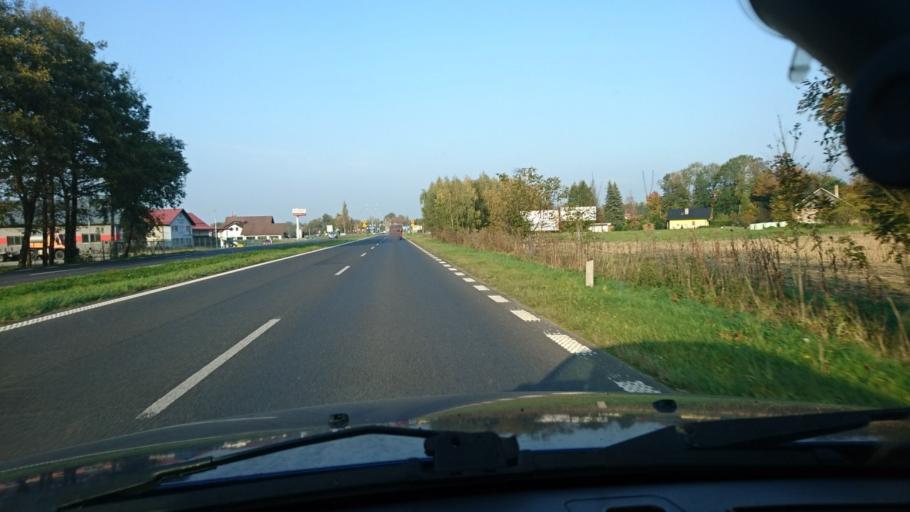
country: PL
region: Silesian Voivodeship
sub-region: Powiat cieszynski
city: Ustron
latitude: 49.7557
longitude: 18.8007
